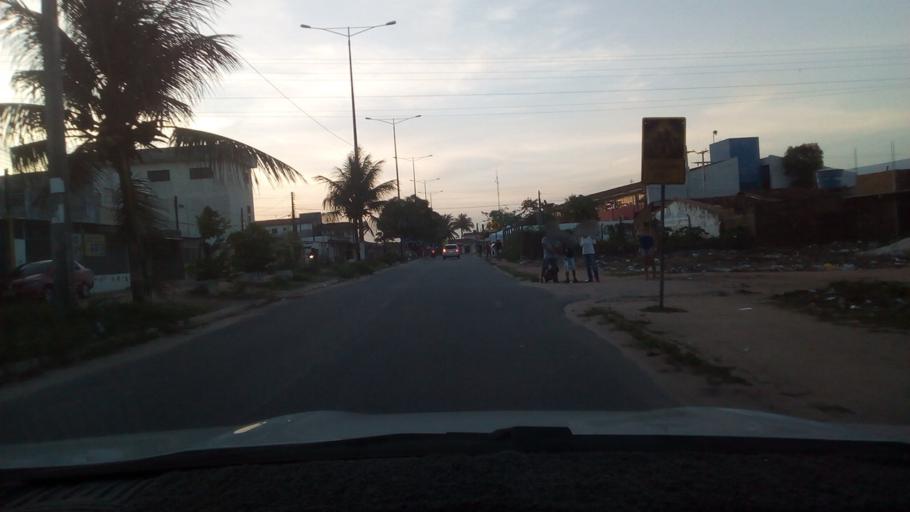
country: BR
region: Paraiba
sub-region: Bayeux
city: Bayeux
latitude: -7.1746
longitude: -34.9286
